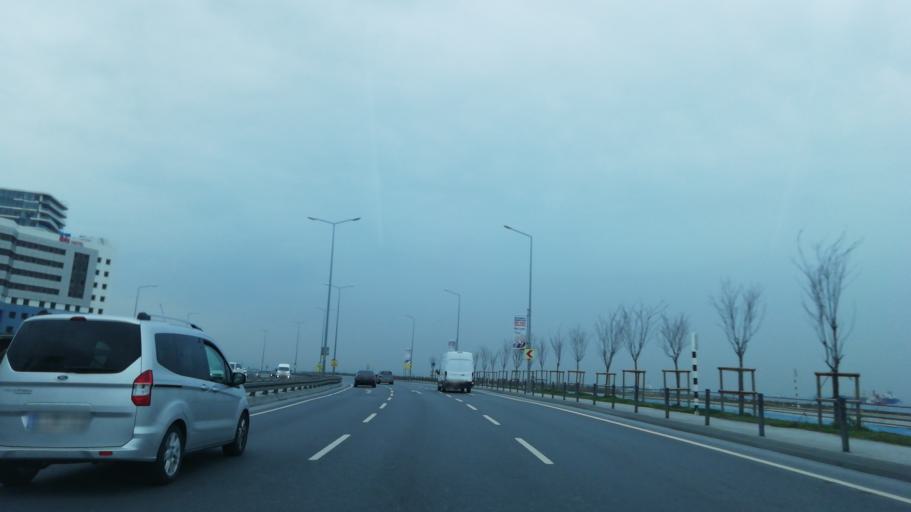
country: TR
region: Istanbul
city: Zeytinburnu
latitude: 40.9792
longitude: 28.9008
